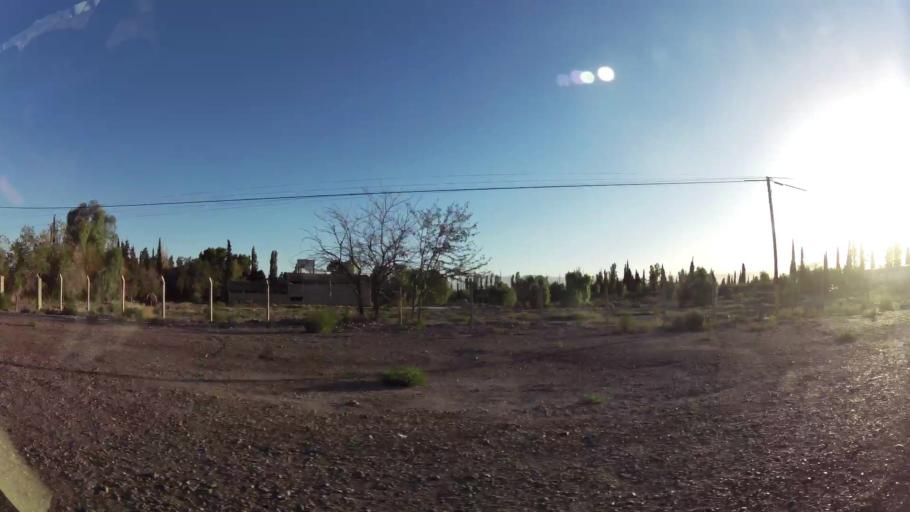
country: AR
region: San Juan
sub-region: Departamento de Santa Lucia
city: Santa Lucia
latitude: -31.5477
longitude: -68.4862
